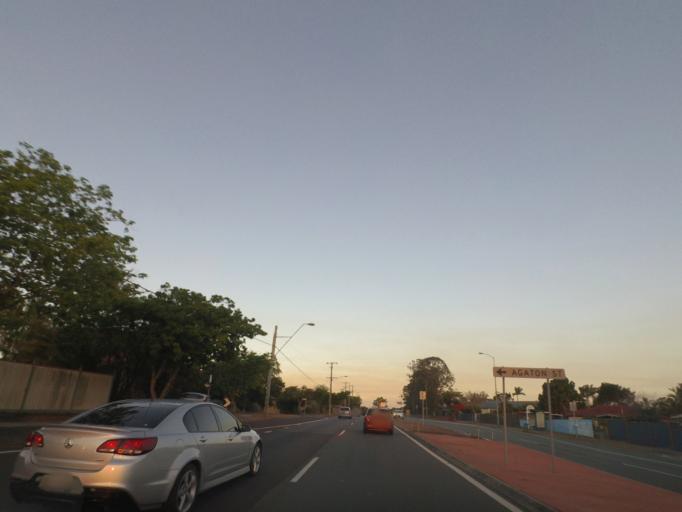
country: AU
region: Queensland
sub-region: Brisbane
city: Upper Mount Gravatt
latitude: -27.5550
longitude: 153.0977
